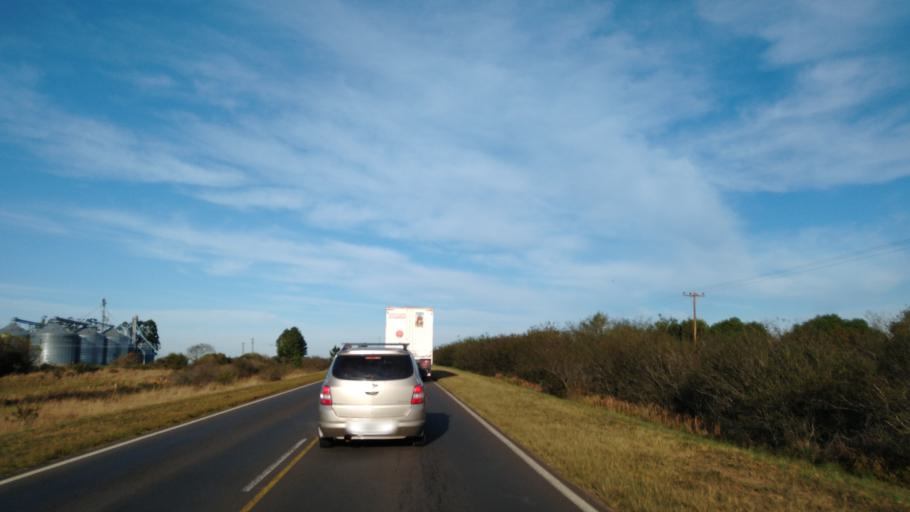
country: AR
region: Corrientes
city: La Cruz
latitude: -29.2073
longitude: -56.6982
